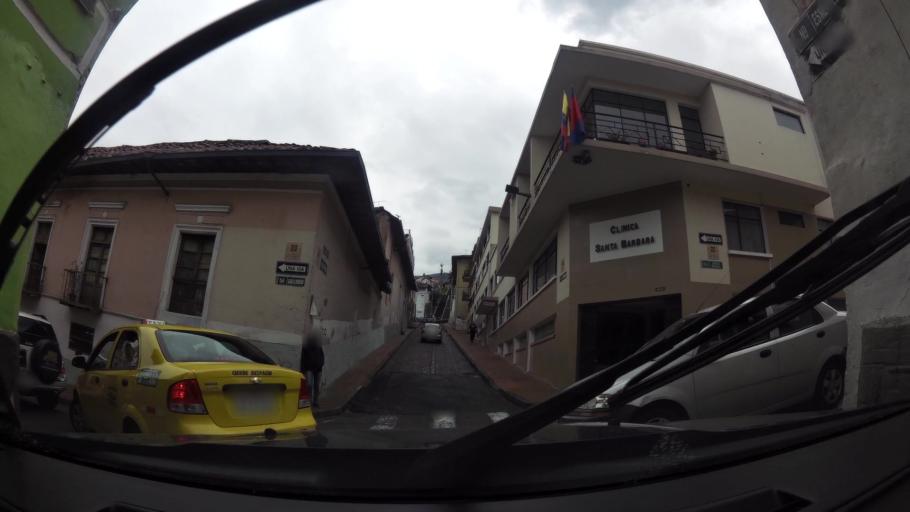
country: EC
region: Pichincha
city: Quito
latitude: -0.2169
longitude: -78.5099
